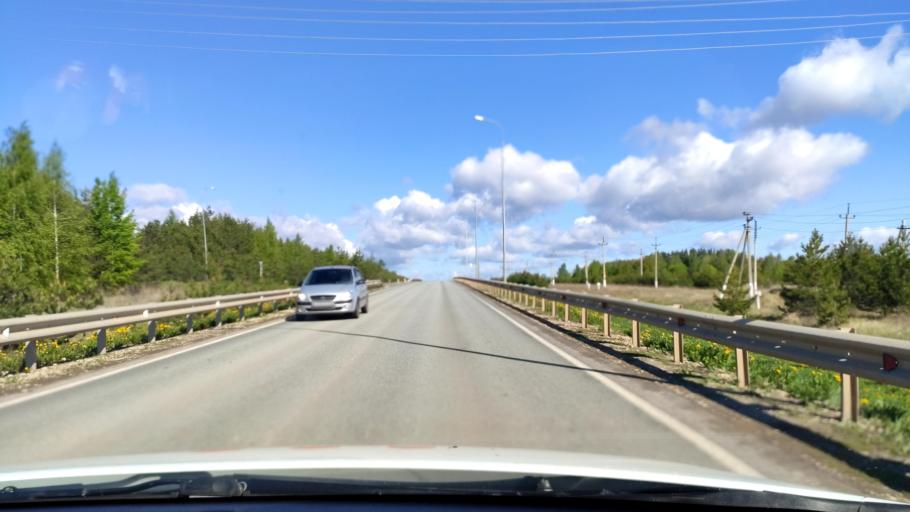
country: RU
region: Tatarstan
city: Sviyazhsk
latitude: 55.7297
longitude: 48.7443
